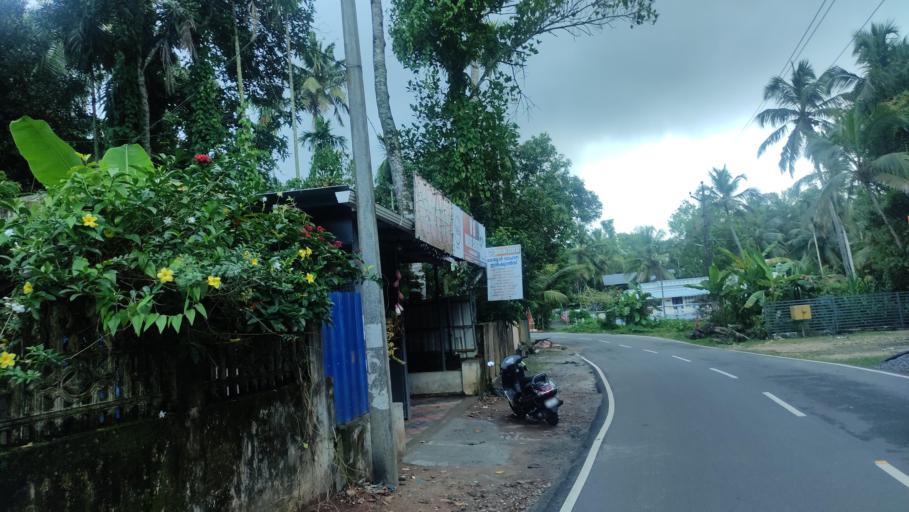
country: IN
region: Kerala
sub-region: Alappuzha
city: Kayankulam
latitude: 9.1944
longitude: 76.5018
